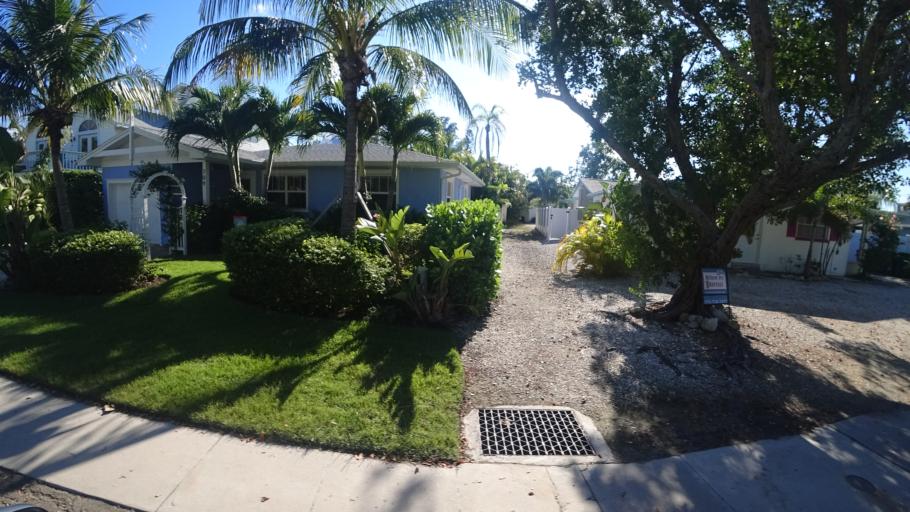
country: US
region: Florida
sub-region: Manatee County
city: Anna Maria
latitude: 27.5373
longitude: -82.7413
